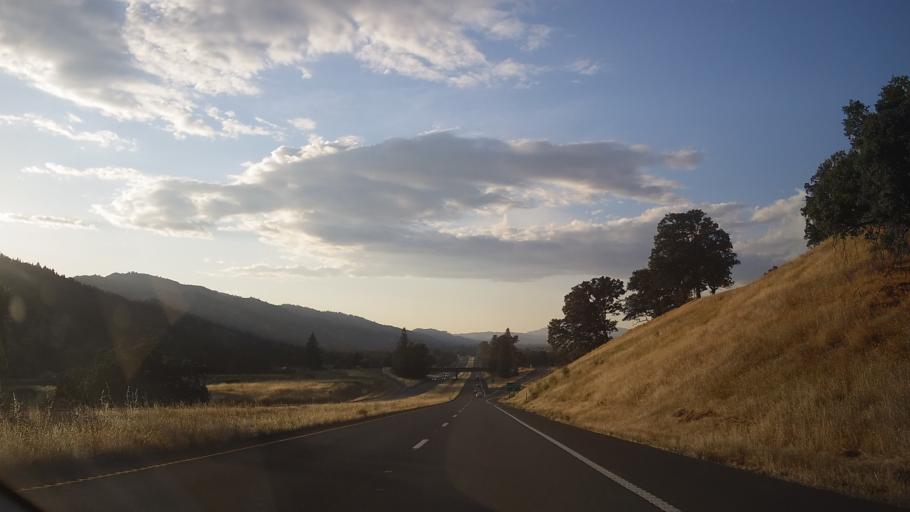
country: US
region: California
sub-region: Mendocino County
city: Talmage
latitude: 39.0798
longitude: -123.1797
